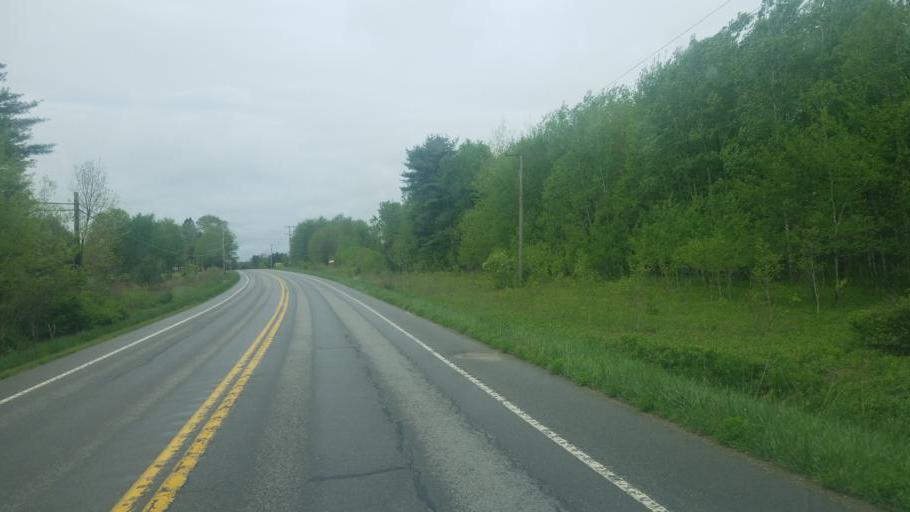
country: US
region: Pennsylvania
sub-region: Forest County
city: Marienville
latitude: 41.4470
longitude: -79.1743
